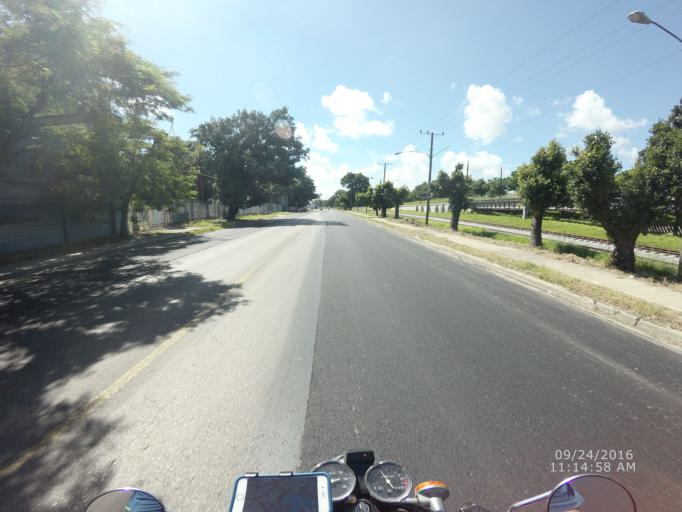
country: CU
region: La Habana
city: La Habana Vieja
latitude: 23.1211
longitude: -82.3597
